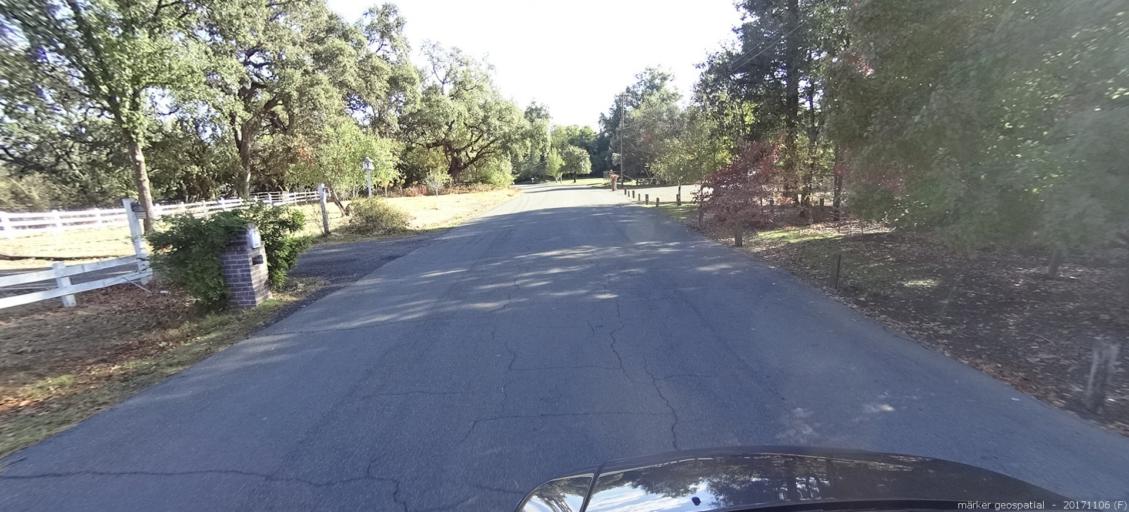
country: US
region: California
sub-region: Shasta County
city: Palo Cedro
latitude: 40.5432
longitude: -122.2453
